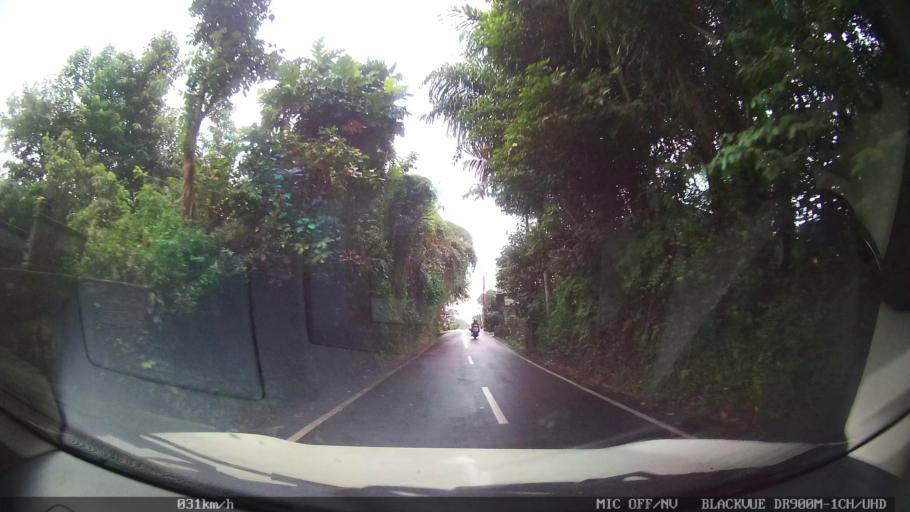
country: ID
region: Bali
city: Banjar Kembangsari
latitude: -8.5127
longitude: 115.2057
